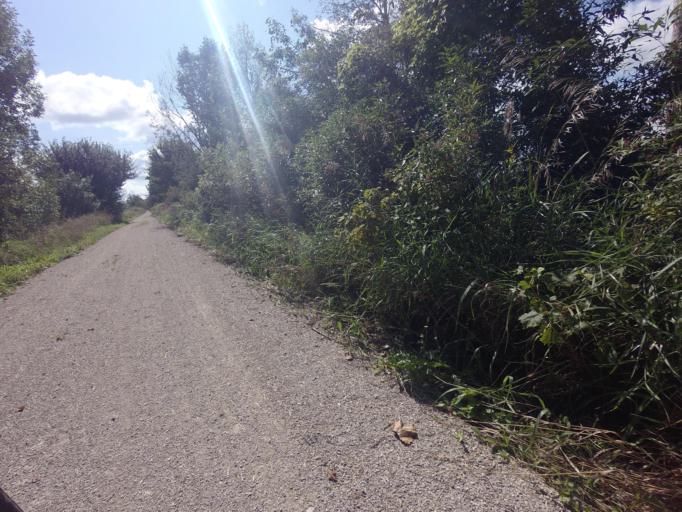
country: CA
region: Ontario
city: Huron East
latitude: 43.6971
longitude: -81.3406
